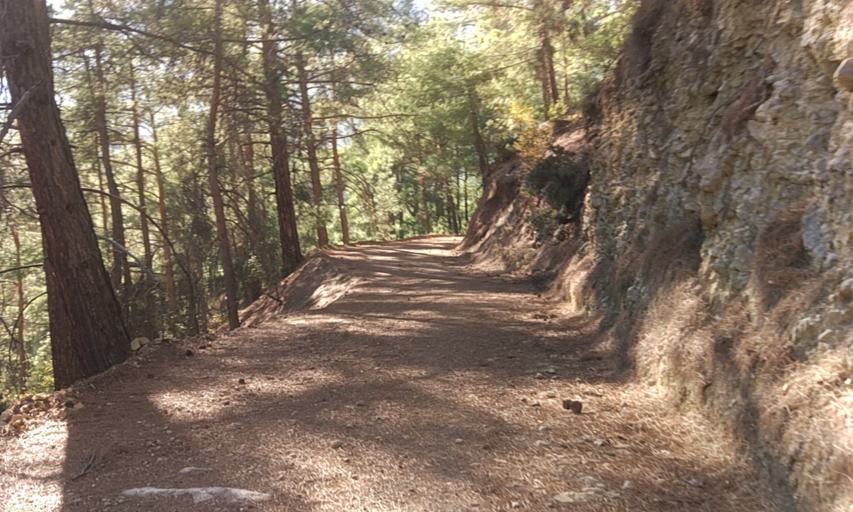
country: TR
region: Antalya
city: Altinyaka
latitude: 36.6049
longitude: 30.4325
